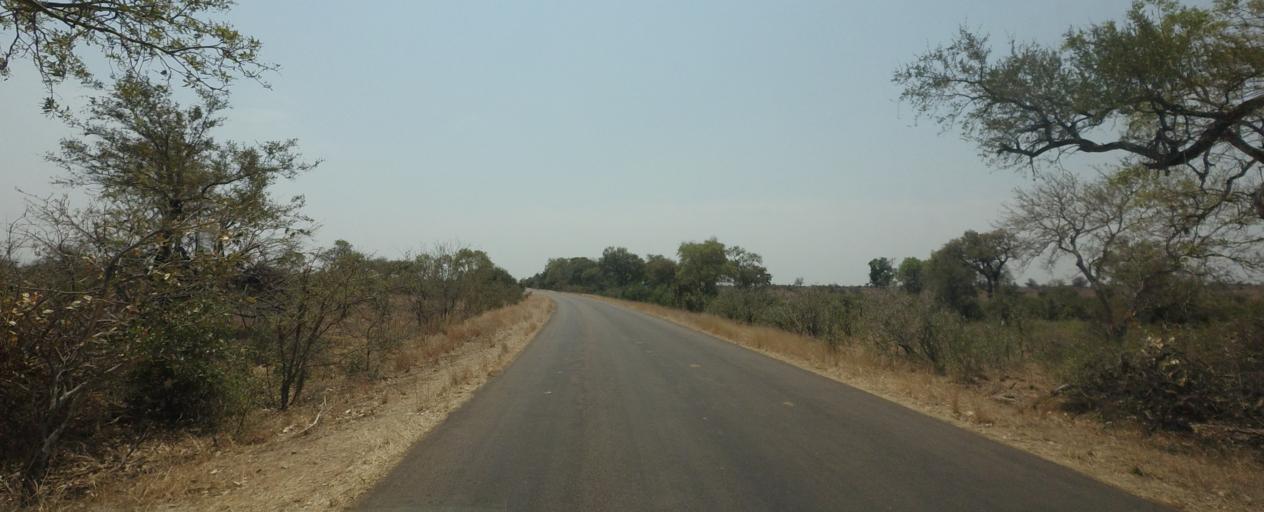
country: ZA
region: Limpopo
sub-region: Mopani District Municipality
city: Phalaborwa
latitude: -24.1642
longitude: 31.7201
